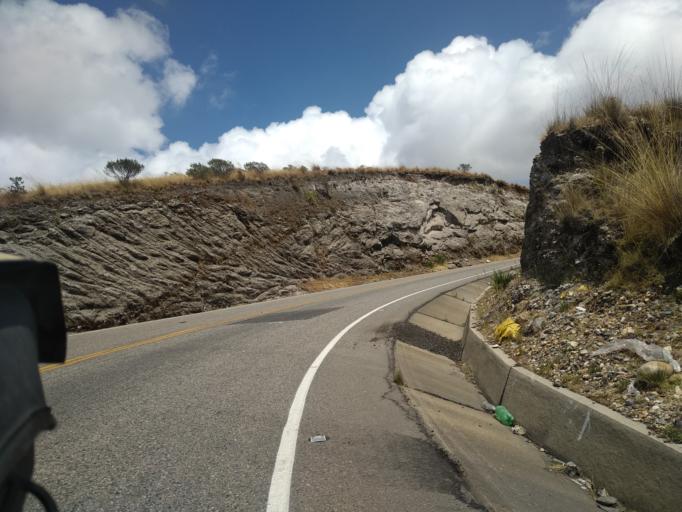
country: PE
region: La Libertad
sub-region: Provincia de Santiago de Chuco
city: Quiruvilca
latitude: -7.9253
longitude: -78.1524
